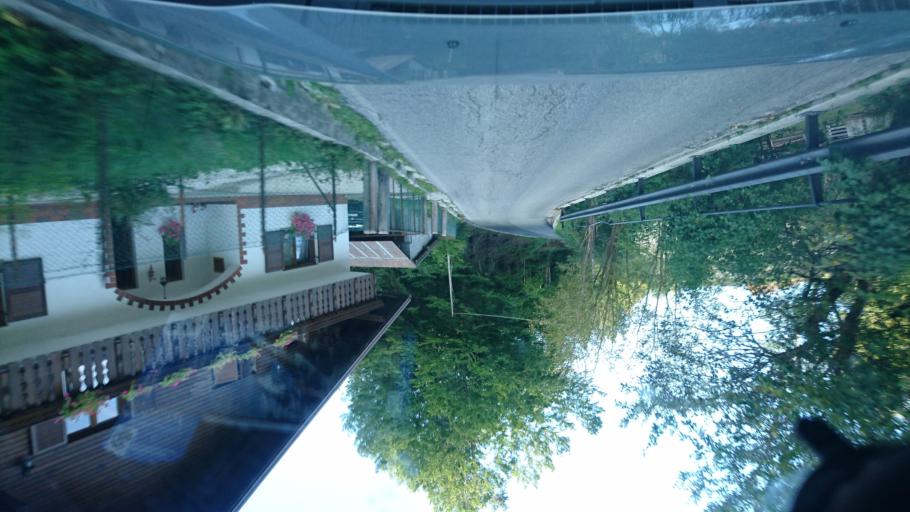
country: AT
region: Carinthia
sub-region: Politischer Bezirk Villach Land
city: Hohenthurn
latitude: 46.4948
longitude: 13.6624
